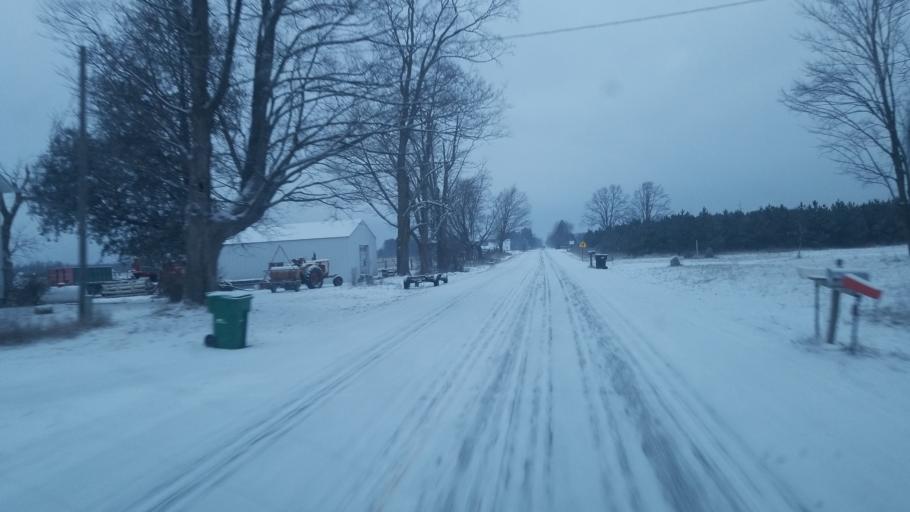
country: US
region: Michigan
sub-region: Osceola County
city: Reed City
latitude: 43.8237
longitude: -85.4241
